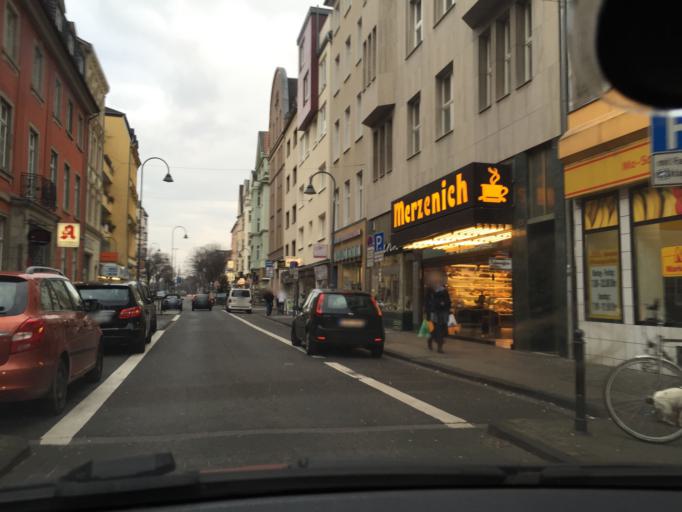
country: DE
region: North Rhine-Westphalia
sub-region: Regierungsbezirk Koln
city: Deutz
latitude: 50.9368
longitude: 6.9755
